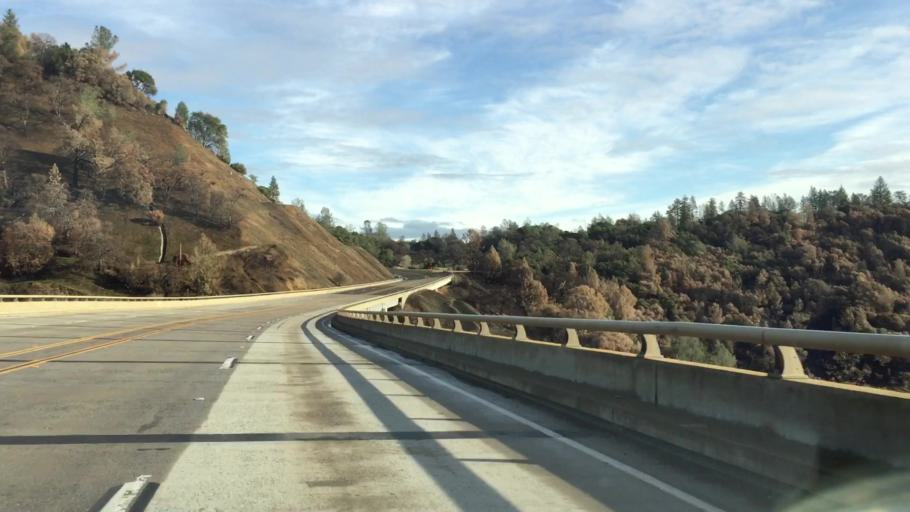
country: US
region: California
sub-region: Butte County
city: Berry Creek
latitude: 39.6669
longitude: -121.5303
